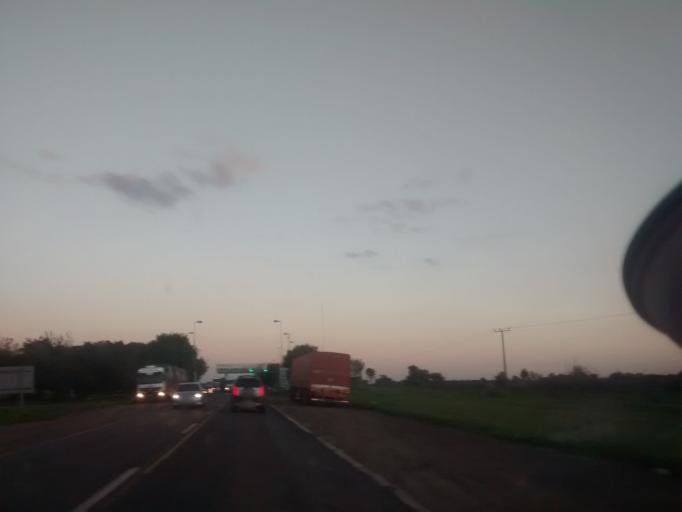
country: AR
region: Chaco
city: Makalle
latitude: -27.1854
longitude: -59.3278
